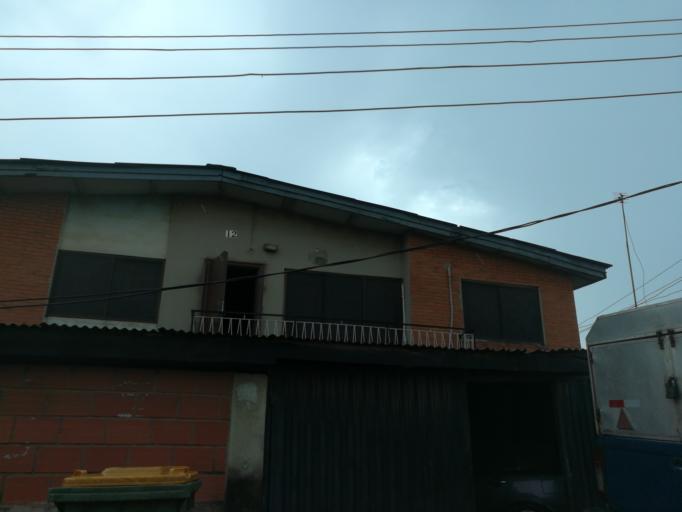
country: NG
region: Lagos
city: Oshodi
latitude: 6.5585
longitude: 3.3390
